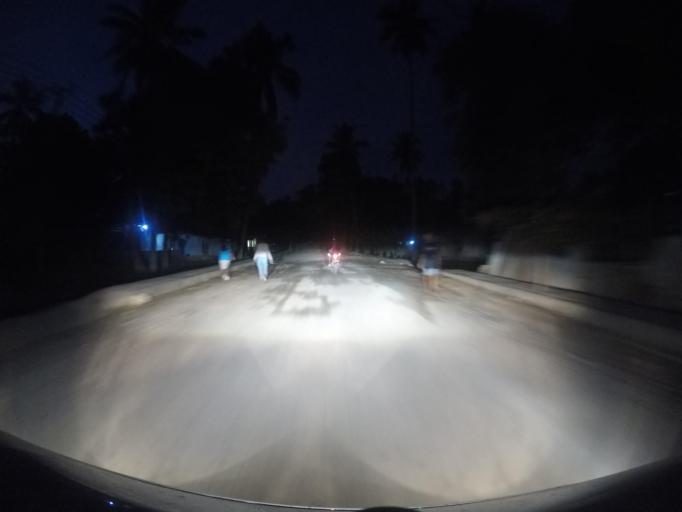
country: TL
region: Viqueque
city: Viqueque
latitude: -8.8482
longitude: 126.3668
